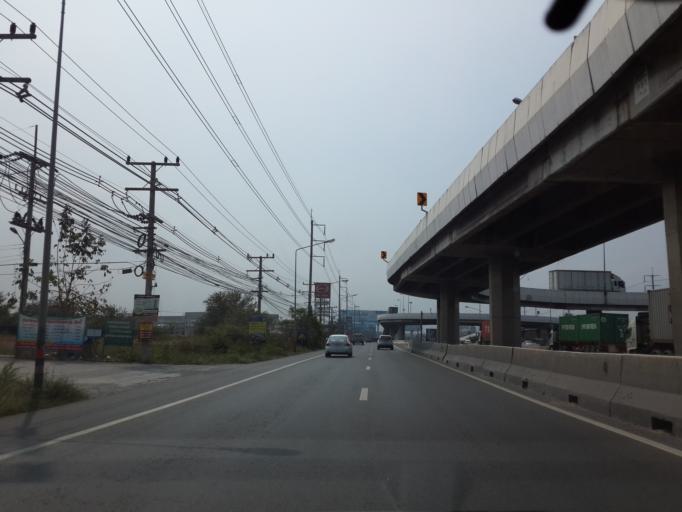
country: TH
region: Chon Buri
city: Chon Buri
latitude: 13.4354
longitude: 101.0020
